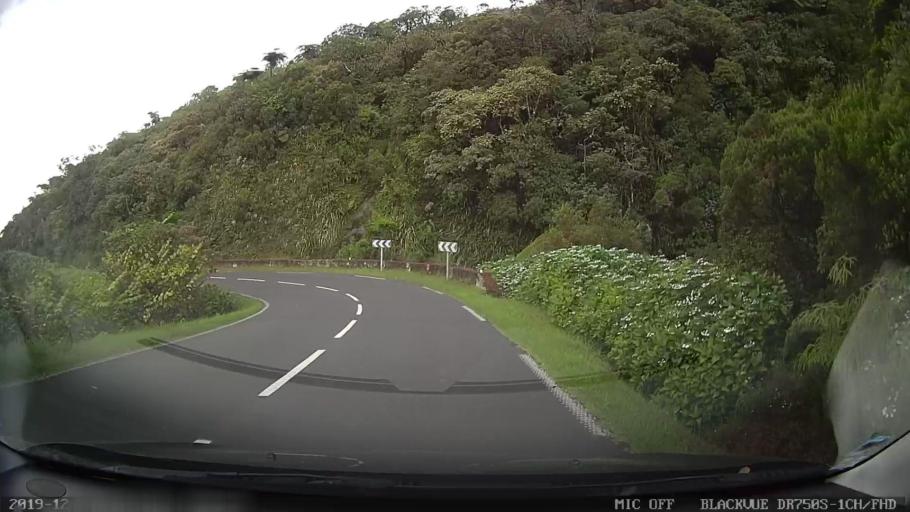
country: RE
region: Reunion
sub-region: Reunion
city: Cilaos
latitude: -21.1628
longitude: 55.5959
